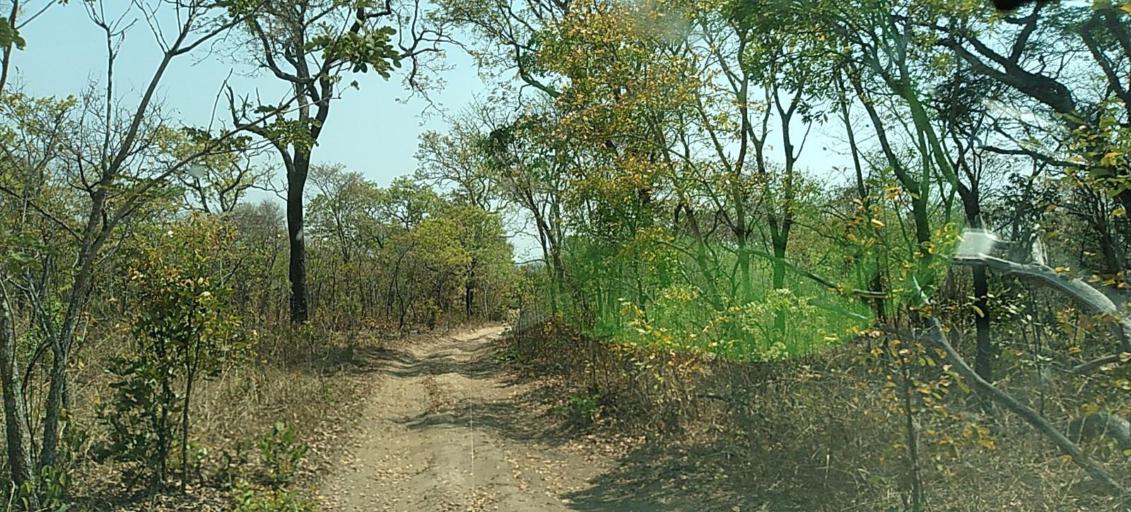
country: ZM
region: North-Western
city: Kalengwa
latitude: -13.1130
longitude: 24.6905
